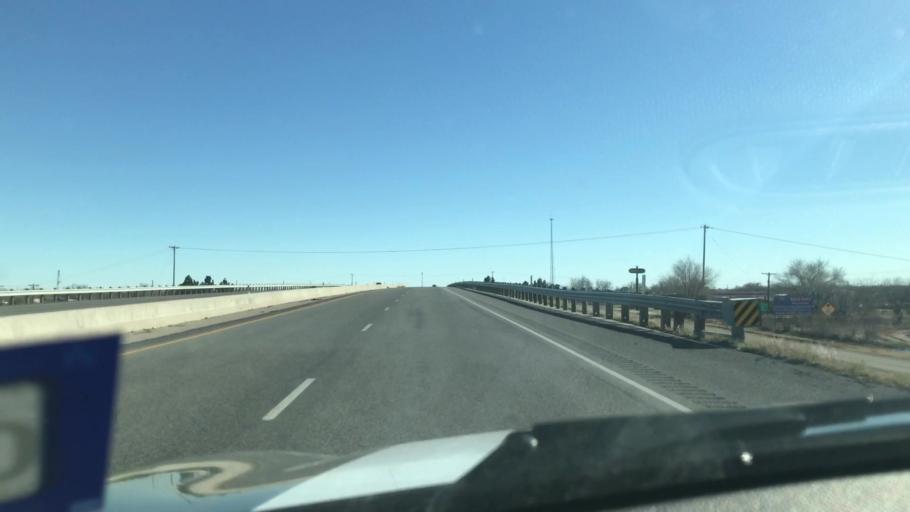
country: US
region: Texas
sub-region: Scurry County
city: Snyder
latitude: 32.7508
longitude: -100.9263
